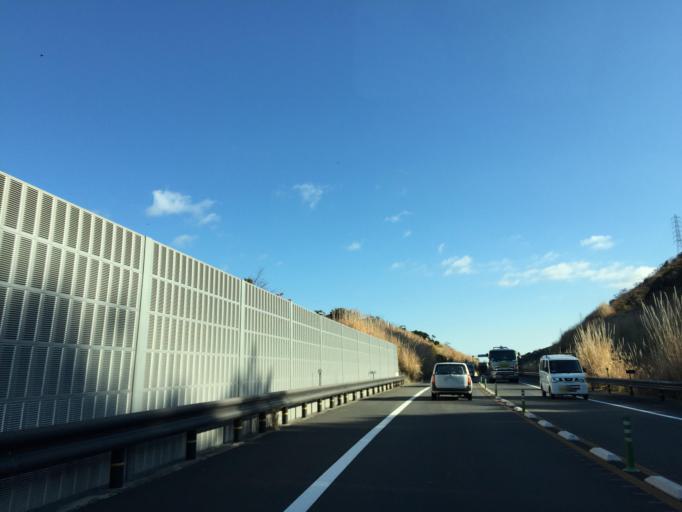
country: JP
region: Wakayama
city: Wakayama-shi
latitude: 34.3188
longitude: 135.1641
